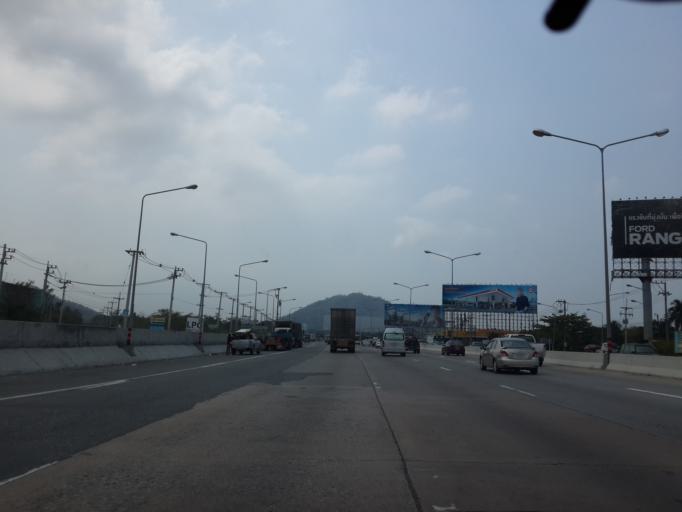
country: TH
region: Chon Buri
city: Chon Buri
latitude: 13.2949
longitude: 100.9933
